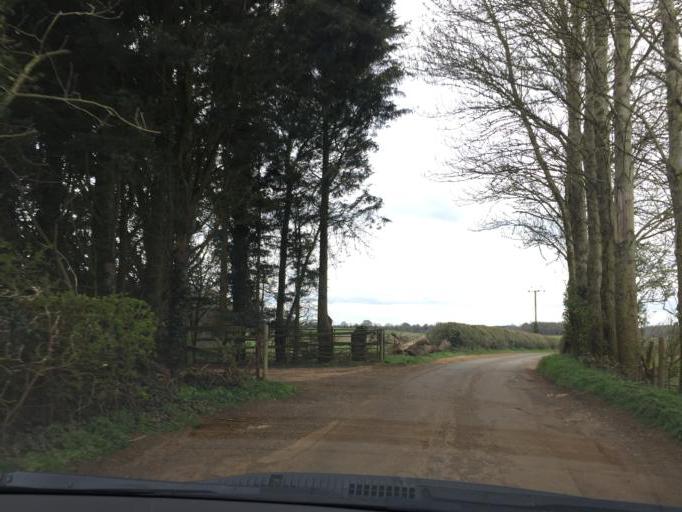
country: GB
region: England
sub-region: Oxfordshire
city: Hanwell
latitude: 52.0869
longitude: -1.3771
